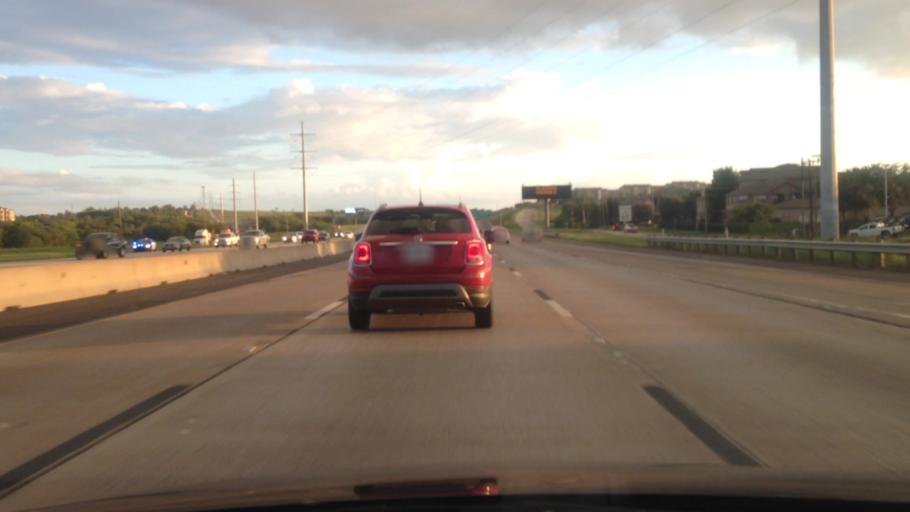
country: US
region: Texas
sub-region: Tarrant County
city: White Settlement
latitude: 32.7557
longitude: -97.4789
